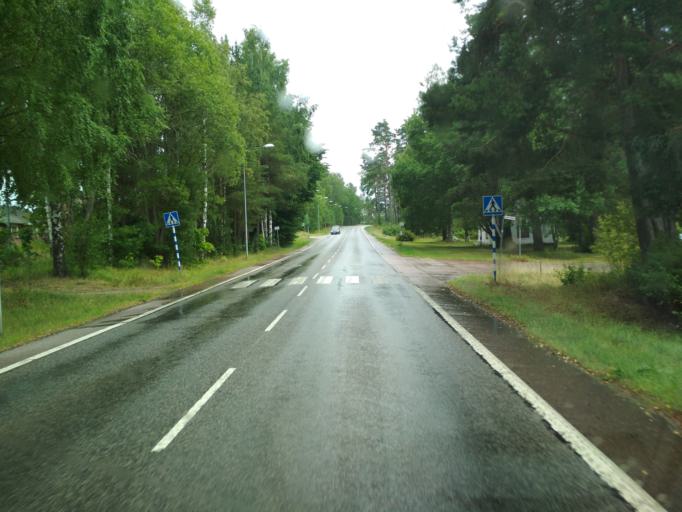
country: SE
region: Vaestmanland
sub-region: Surahammars Kommun
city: Ramnas
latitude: 59.7713
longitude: 16.2003
